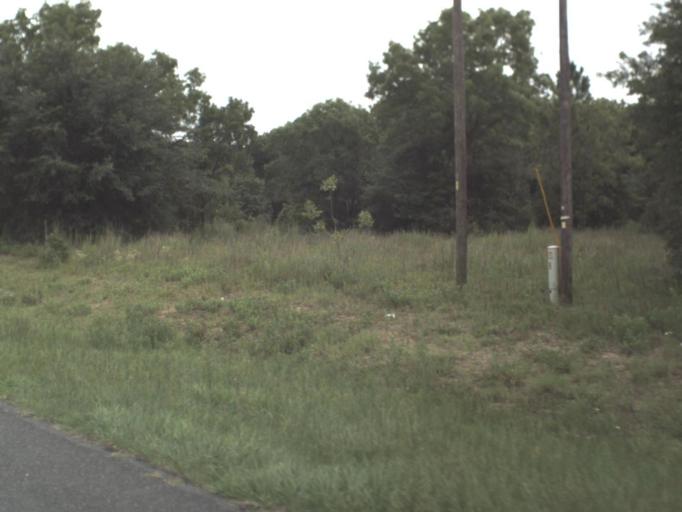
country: US
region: Florida
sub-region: Levy County
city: Williston Highlands
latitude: 29.2245
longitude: -82.4410
